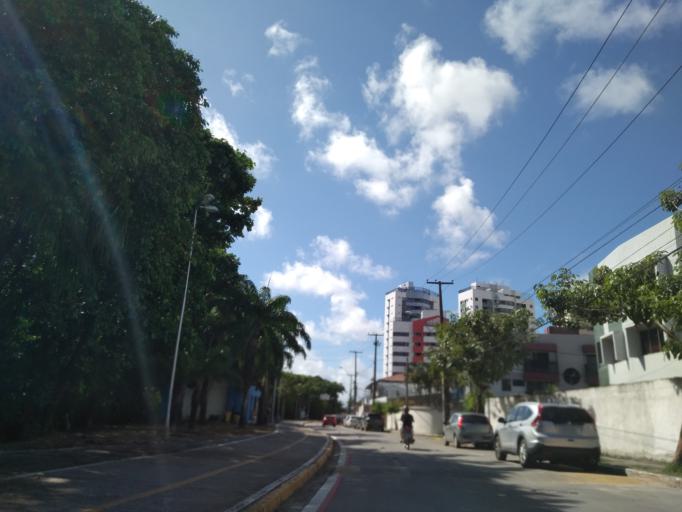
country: BR
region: Pernambuco
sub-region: Recife
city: Recife
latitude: -8.0954
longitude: -34.9134
